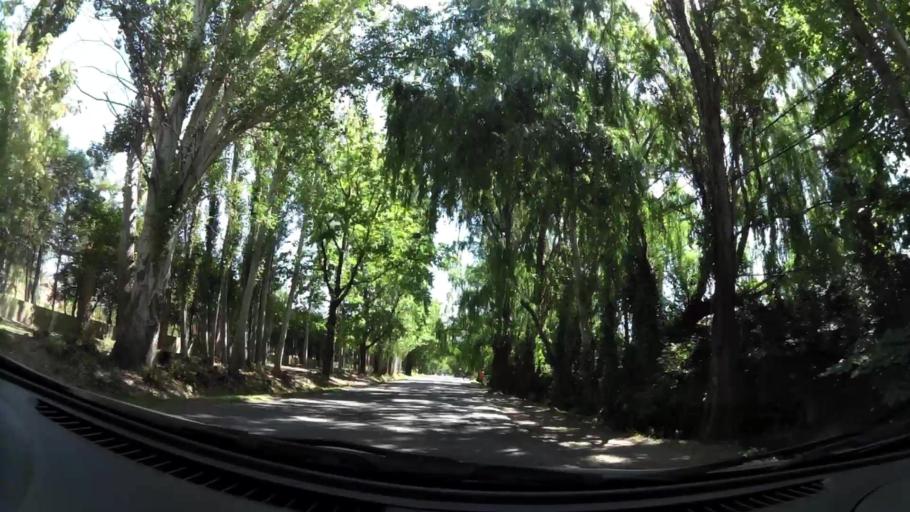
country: AR
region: Mendoza
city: Lujan de Cuyo
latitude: -32.9836
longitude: -68.8542
